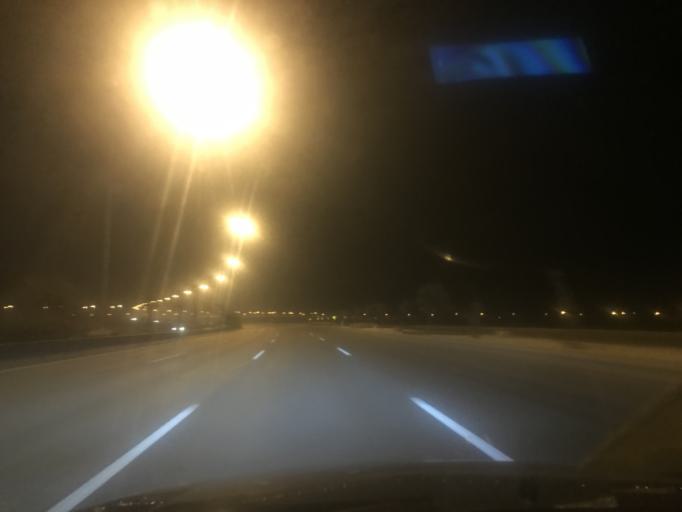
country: SA
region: Ar Riyad
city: Riyadh
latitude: 24.8129
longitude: 46.5827
